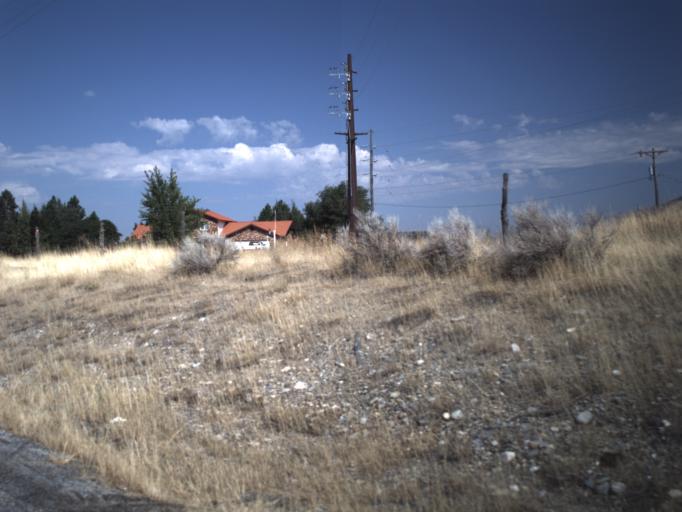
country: US
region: Utah
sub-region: Cache County
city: Hyrum
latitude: 41.6335
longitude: -111.8137
